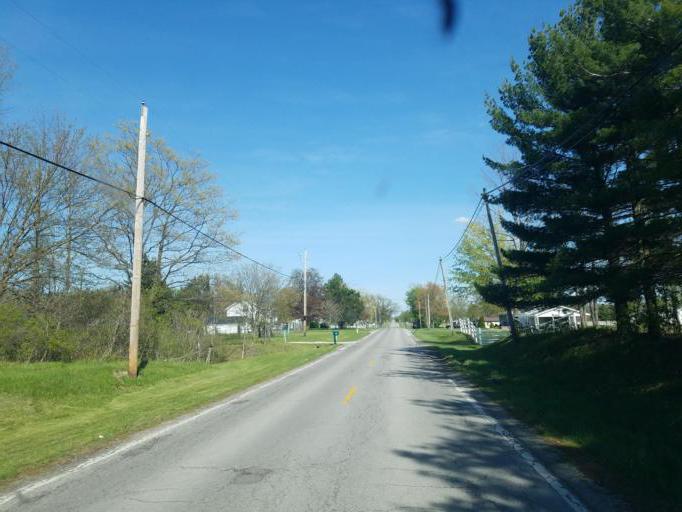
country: US
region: Ohio
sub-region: Huron County
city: Willard
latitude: 41.0690
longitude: -82.7370
